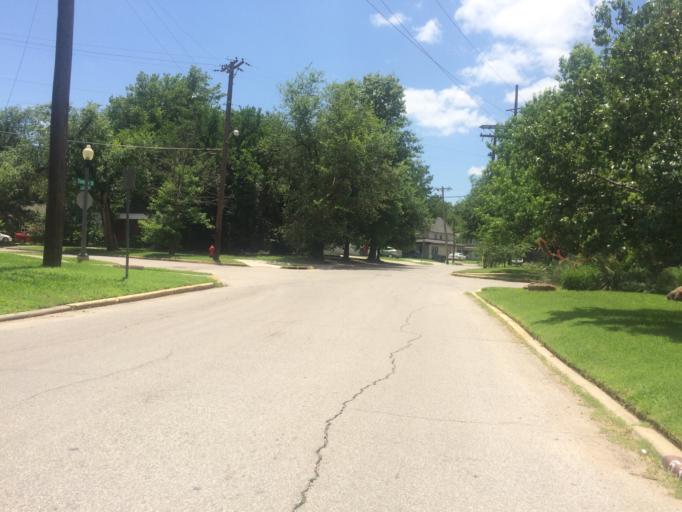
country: US
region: Oklahoma
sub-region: Cleveland County
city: Norman
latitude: 35.2152
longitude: -97.4488
